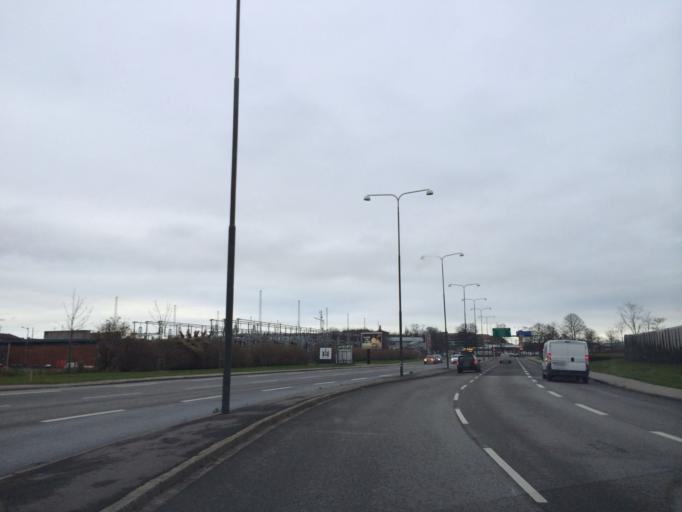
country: SE
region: Skane
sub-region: Malmo
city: Malmoe
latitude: 55.6084
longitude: 13.0225
